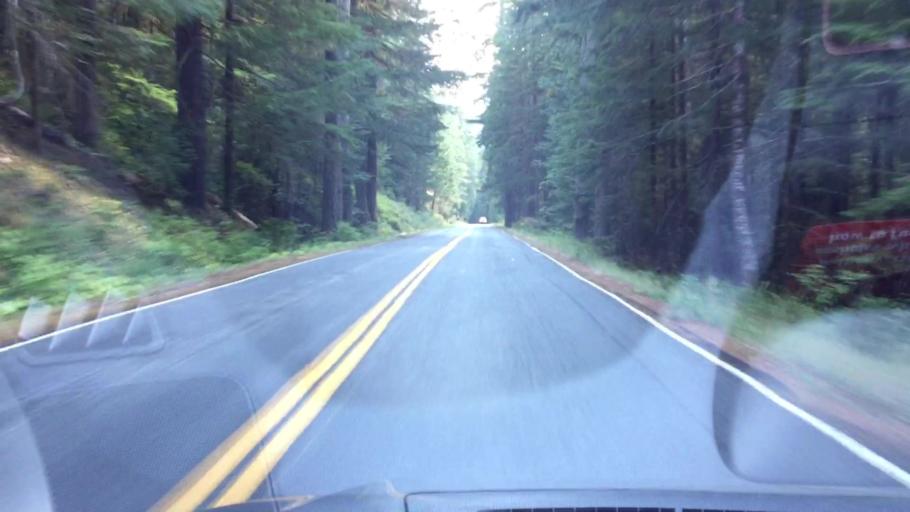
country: US
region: Washington
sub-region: Pierce County
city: Buckley
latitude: 46.7230
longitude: -121.5754
